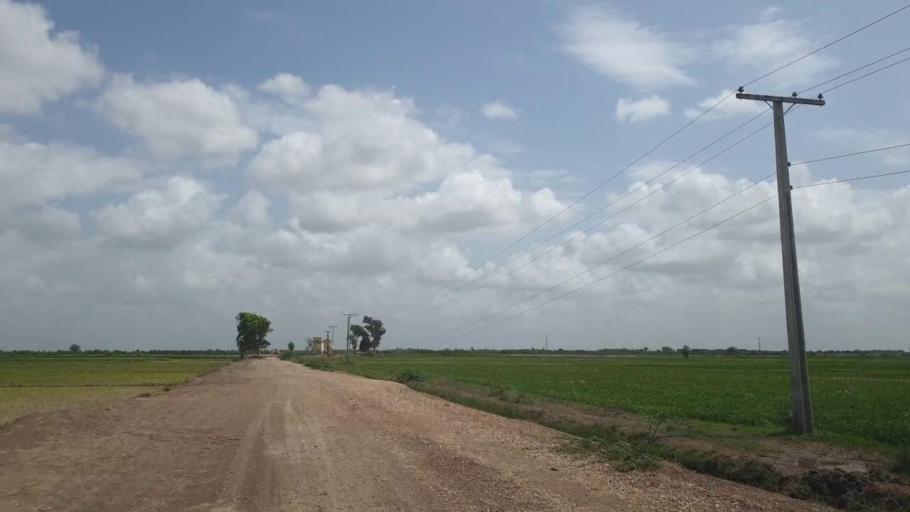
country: PK
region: Sindh
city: Tando Bago
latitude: 24.6491
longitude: 68.9935
